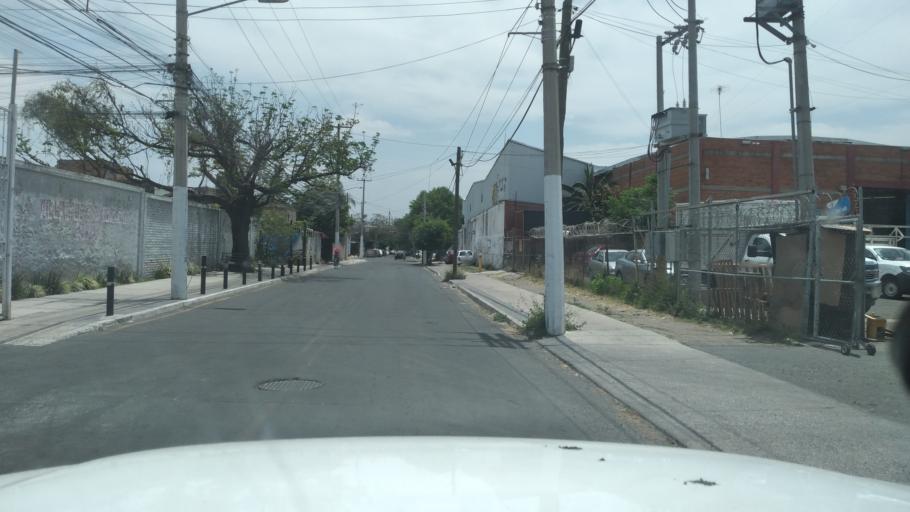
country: MX
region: Jalisco
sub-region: Zapopan
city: Zapopan
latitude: 20.7323
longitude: -103.3713
